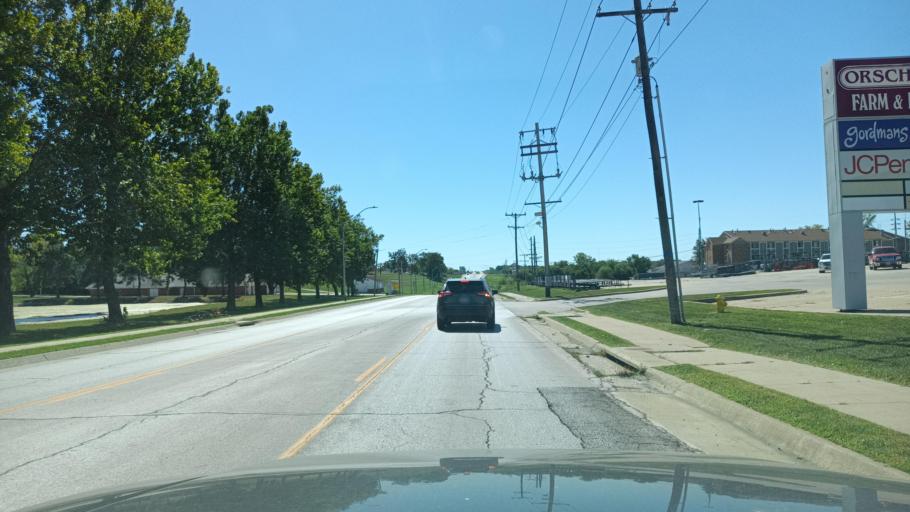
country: US
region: Missouri
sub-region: Adair County
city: Kirksville
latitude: 40.1767
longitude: -92.5720
